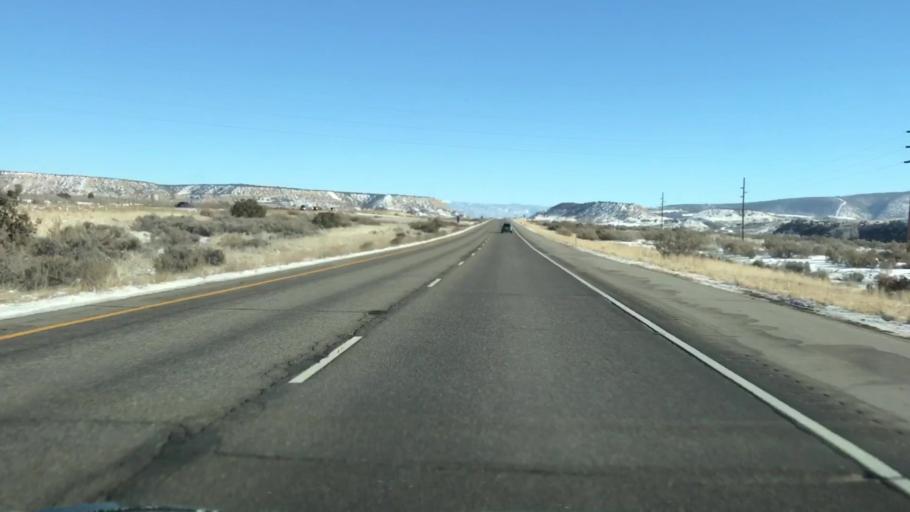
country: US
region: Colorado
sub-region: Garfield County
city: Battlement Mesa
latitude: 39.4989
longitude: -107.9151
